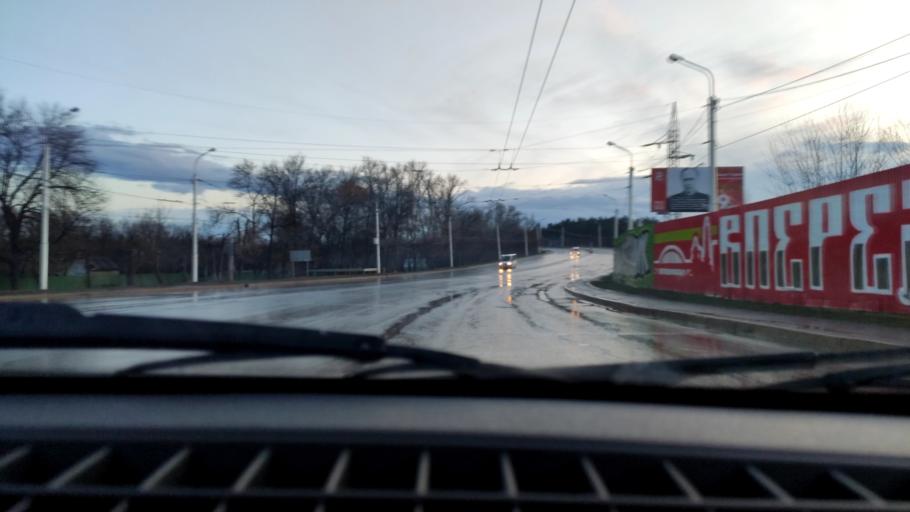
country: RU
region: Bashkortostan
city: Ufa
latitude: 54.8091
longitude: 56.0549
